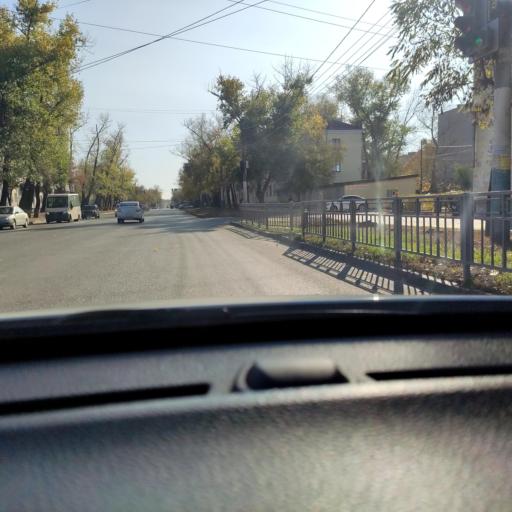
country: RU
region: Voronezj
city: Somovo
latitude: 51.7179
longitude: 39.2740
